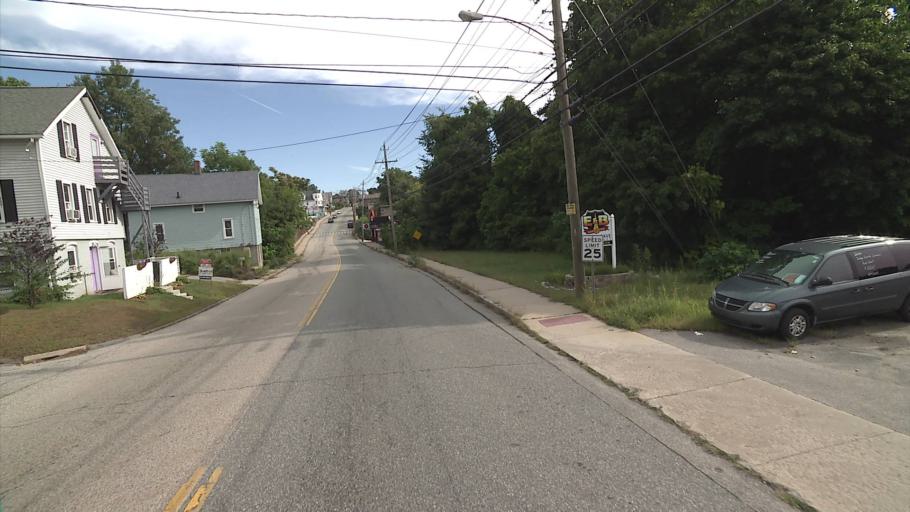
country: US
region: Connecticut
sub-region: New London County
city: Norwich
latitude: 41.5093
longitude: -72.0852
